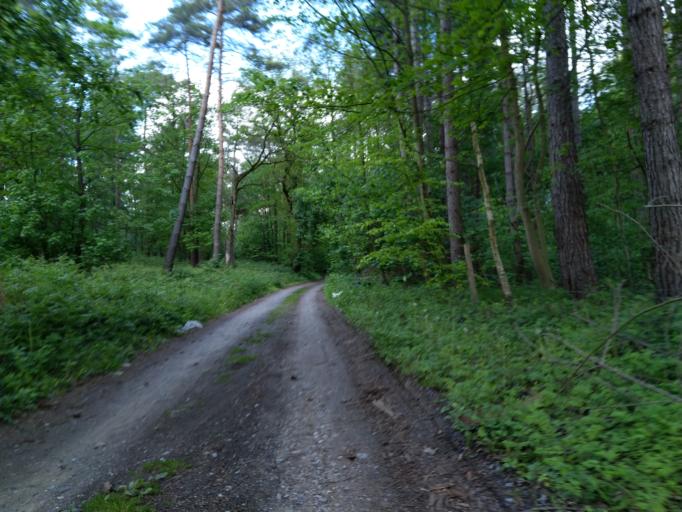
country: BE
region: Wallonia
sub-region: Province du Hainaut
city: Jurbise
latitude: 50.4971
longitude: 3.9232
